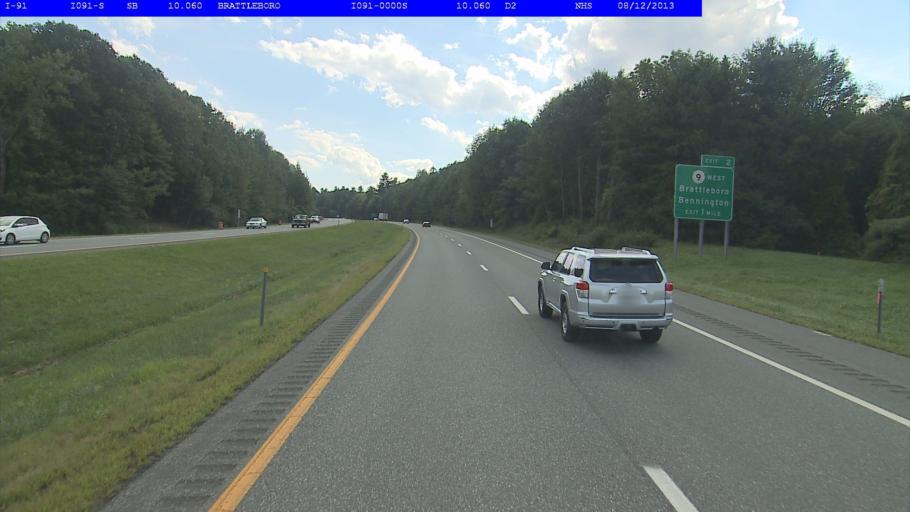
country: US
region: Vermont
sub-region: Windham County
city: Brattleboro
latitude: 42.8694
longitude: -72.5778
